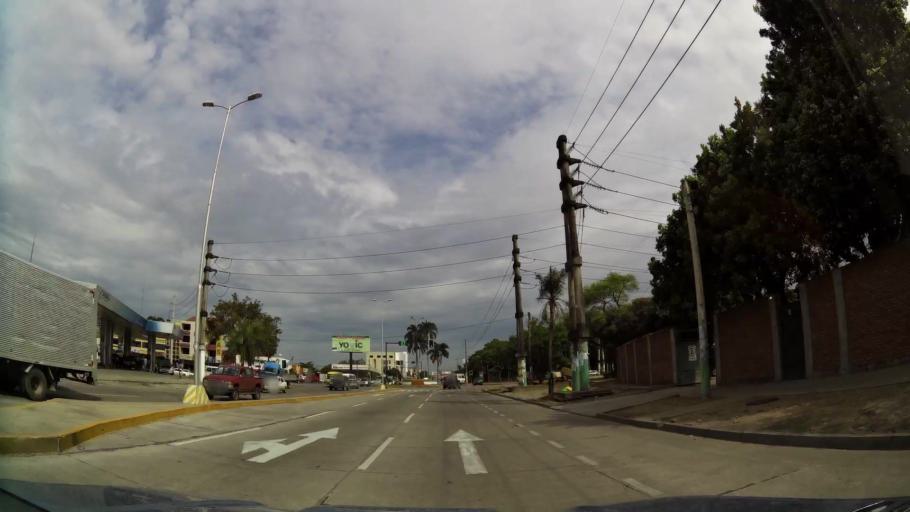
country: BO
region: Santa Cruz
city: Santa Cruz de la Sierra
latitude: -17.7846
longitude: -63.2047
